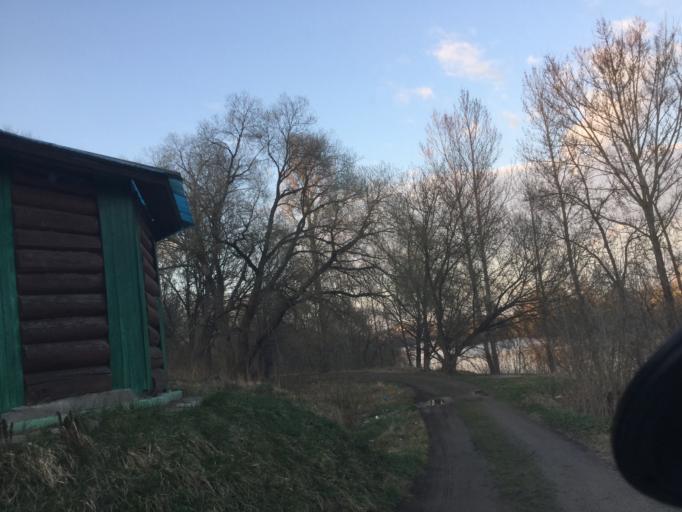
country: BY
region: Vitebsk
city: Vitebsk
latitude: 55.1645
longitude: 30.1317
